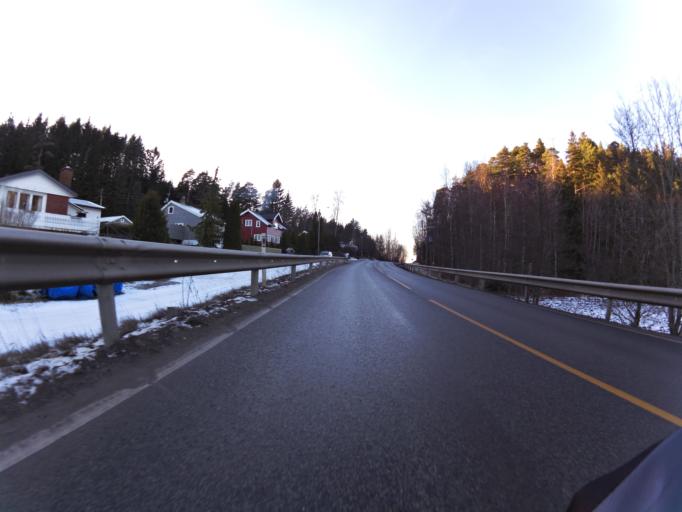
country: NO
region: Ostfold
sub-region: Fredrikstad
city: Fredrikstad
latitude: 59.2474
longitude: 10.8870
